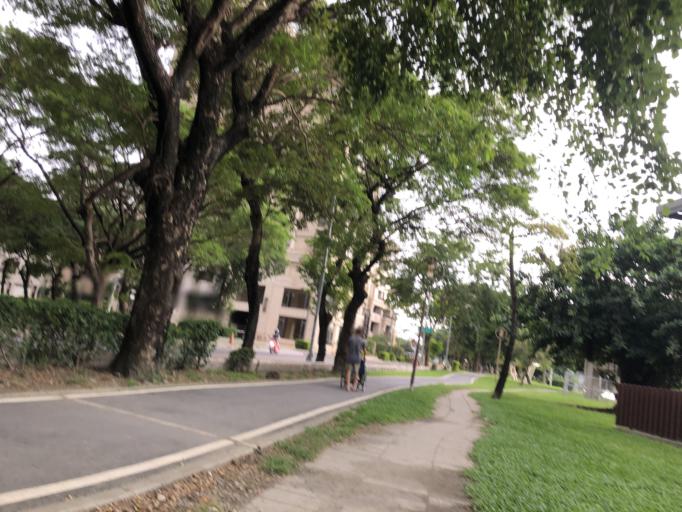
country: TW
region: Kaohsiung
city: Kaohsiung
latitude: 22.6880
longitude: 120.3007
